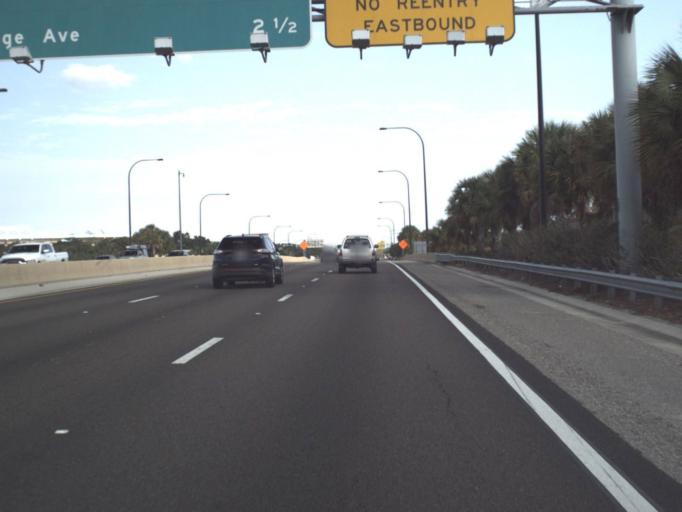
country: US
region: Florida
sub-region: Orange County
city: Orlando
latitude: 28.5432
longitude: -81.4147
